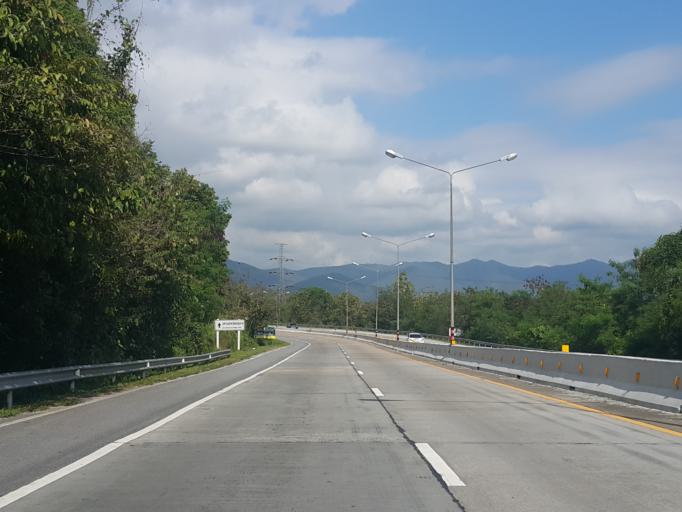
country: TH
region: Lamphun
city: Mae Tha
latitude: 18.4501
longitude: 99.2032
